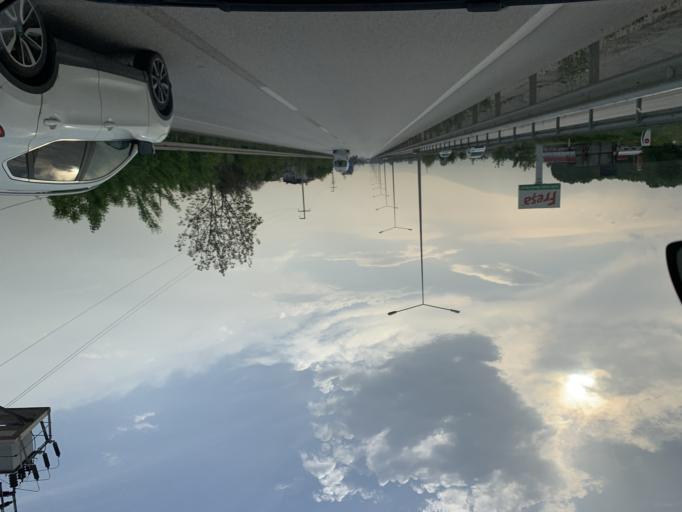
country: TR
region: Bursa
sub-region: Inegoel
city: Inegol
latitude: 40.0619
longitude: 29.5767
